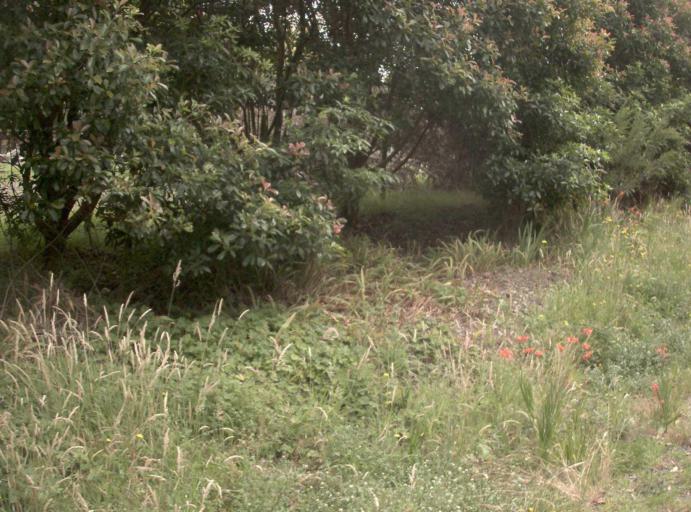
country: AU
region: Victoria
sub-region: Cardinia
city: Koo-Wee-Rup
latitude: -38.3396
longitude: 145.6706
